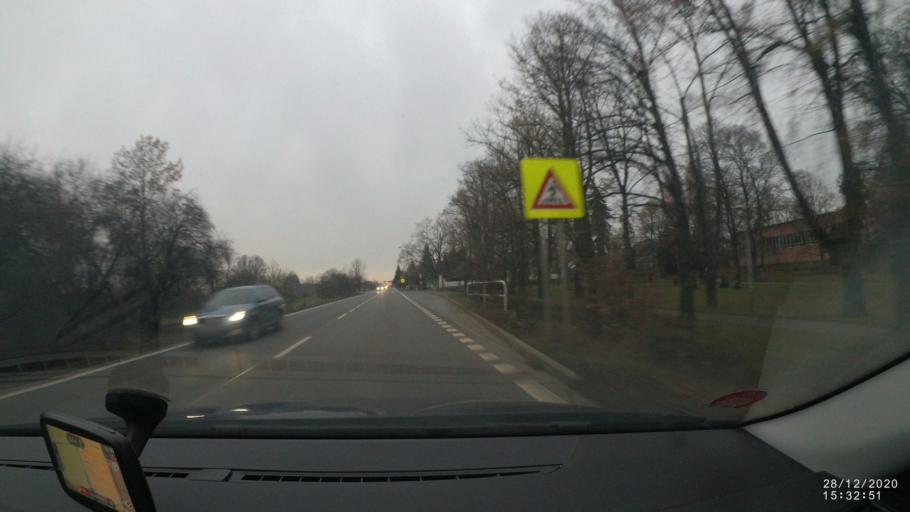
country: CZ
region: Praha
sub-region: Praha 14
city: Hostavice
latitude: 50.0903
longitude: 14.5430
